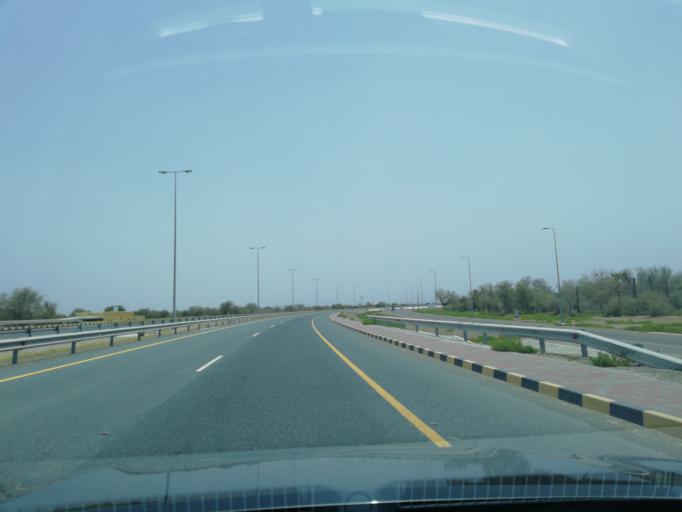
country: OM
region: Al Batinah
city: Shinas
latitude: 24.7534
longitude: 56.4635
